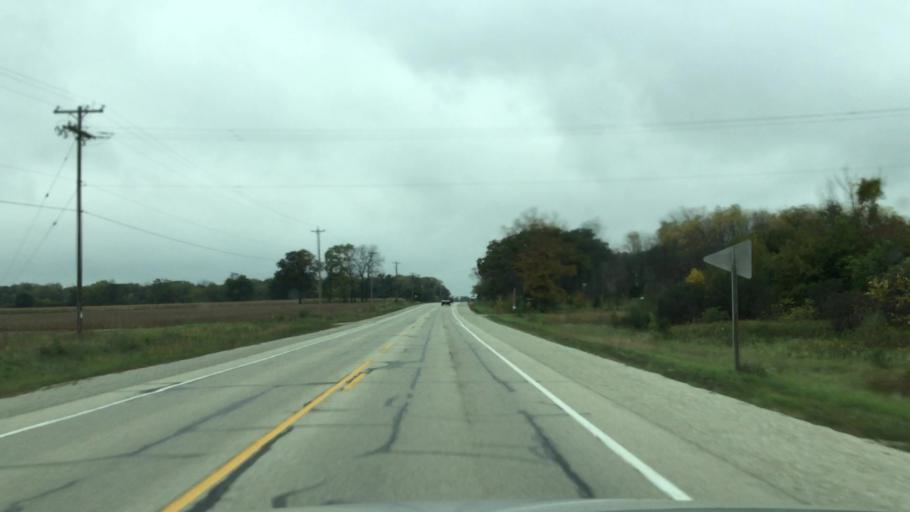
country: US
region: Wisconsin
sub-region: Racine County
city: Eagle Lake
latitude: 42.7427
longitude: -88.1492
